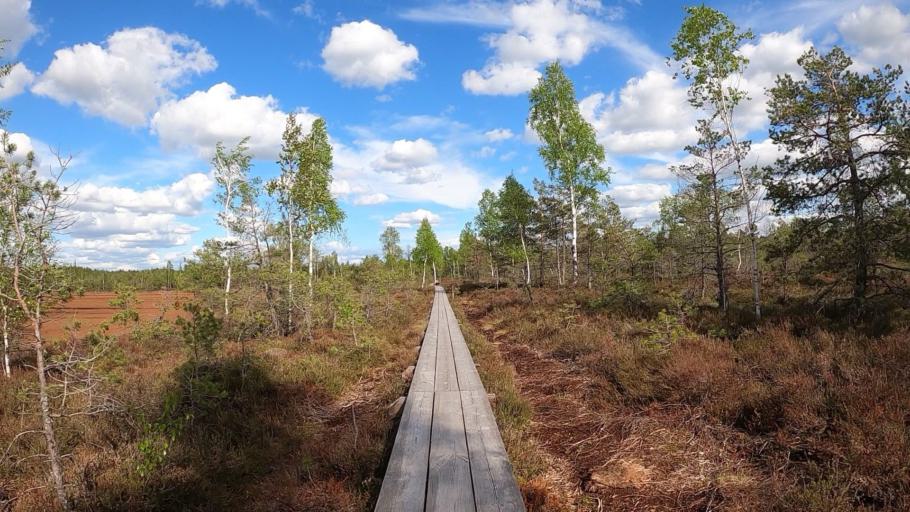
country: LV
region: Jurmala
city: Jurmala
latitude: 56.8577
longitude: 23.8058
